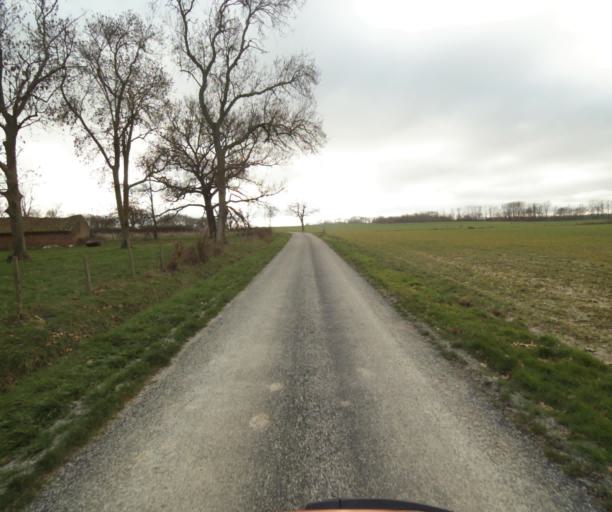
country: FR
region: Midi-Pyrenees
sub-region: Departement de l'Ariege
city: Mazeres
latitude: 43.2273
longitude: 1.7139
